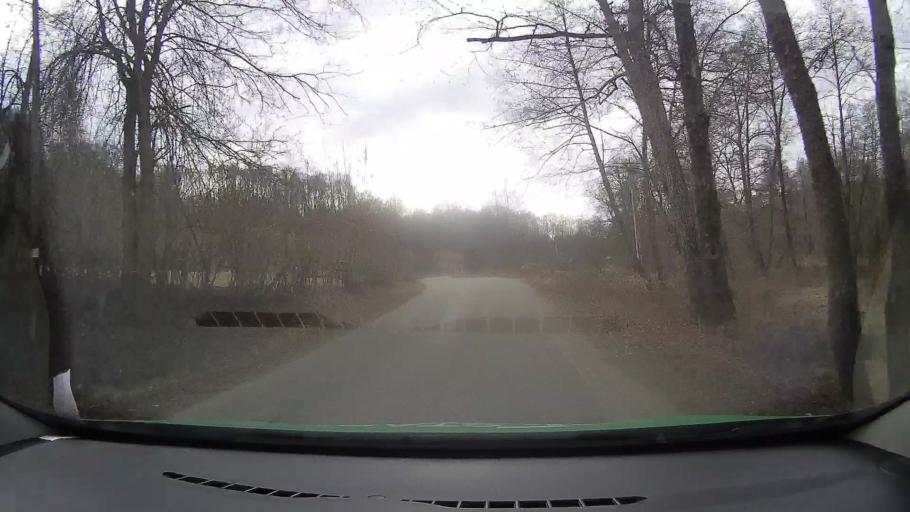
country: RO
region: Dambovita
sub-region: Comuna Valea Lunga
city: Valea Lunga-Cricov
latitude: 45.0848
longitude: 25.5805
